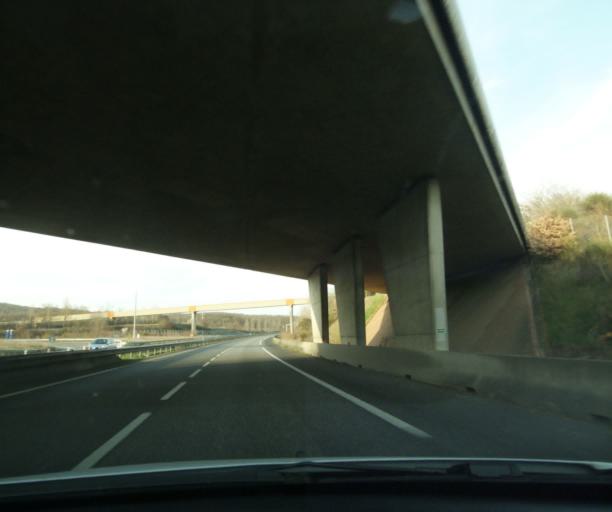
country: FR
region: Midi-Pyrenees
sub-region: Departement de la Haute-Garonne
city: Martres-Tolosane
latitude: 43.1857
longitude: 0.9803
